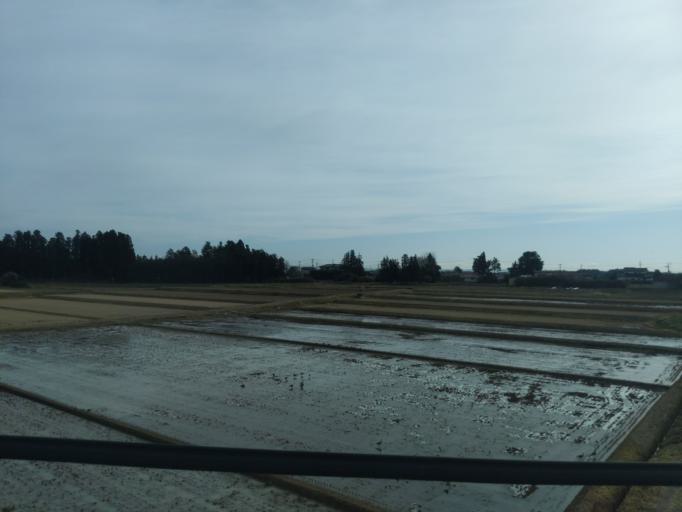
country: JP
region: Iwate
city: Ichinoseki
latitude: 38.7670
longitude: 141.0820
